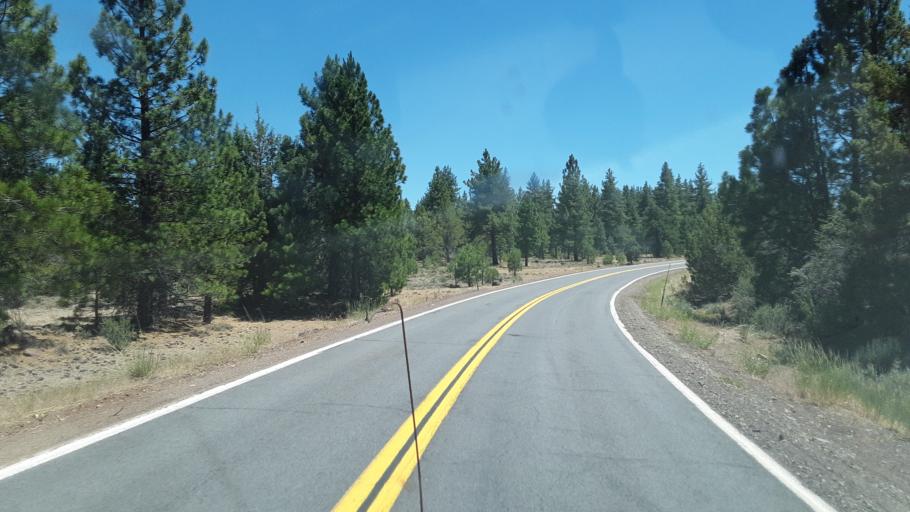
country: US
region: California
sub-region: Lassen County
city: Susanville
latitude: 40.6293
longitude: -120.6433
